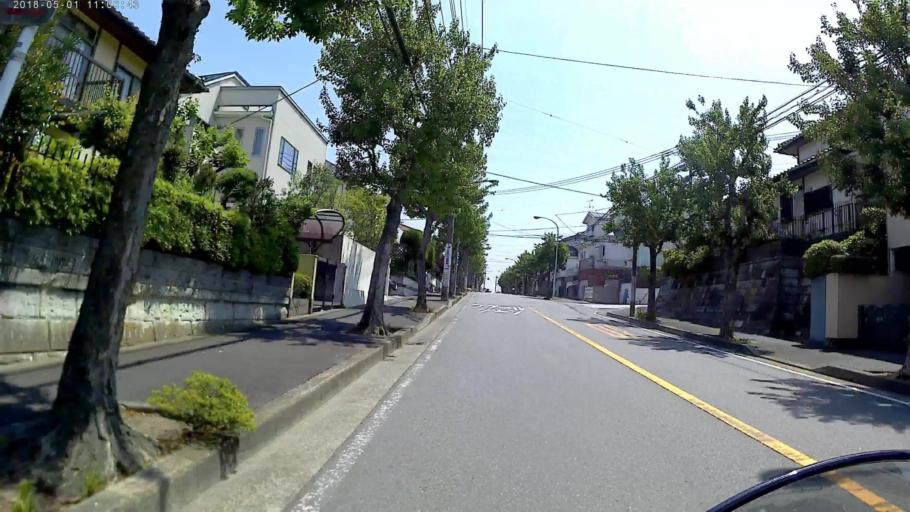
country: JP
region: Kanagawa
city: Minami-rinkan
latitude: 35.4785
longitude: 139.5129
